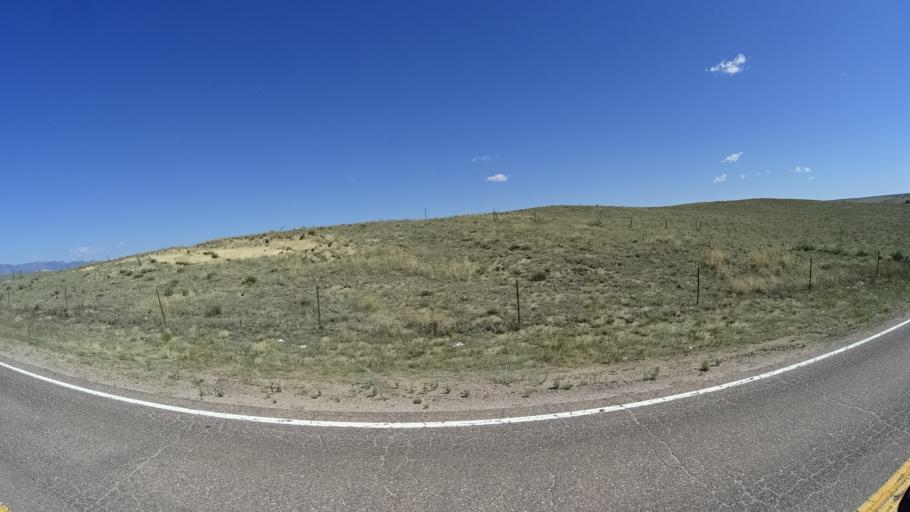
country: US
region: Colorado
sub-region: El Paso County
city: Security-Widefield
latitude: 38.7810
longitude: -104.6214
